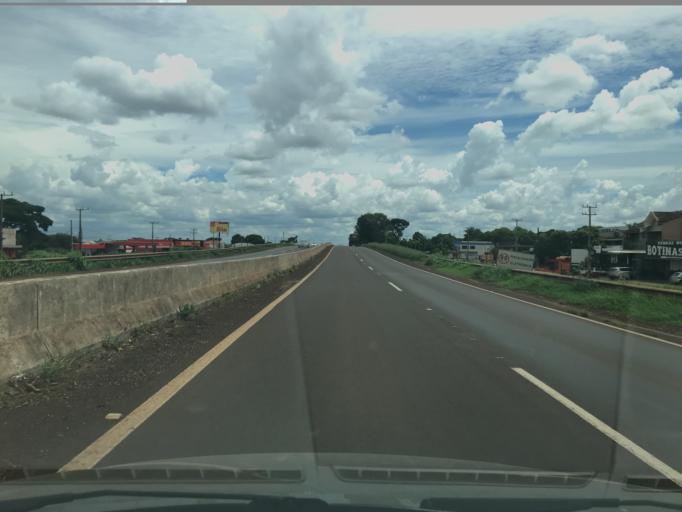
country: BR
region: Parana
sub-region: Paicandu
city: Paicandu
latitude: -23.4594
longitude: -52.0303
